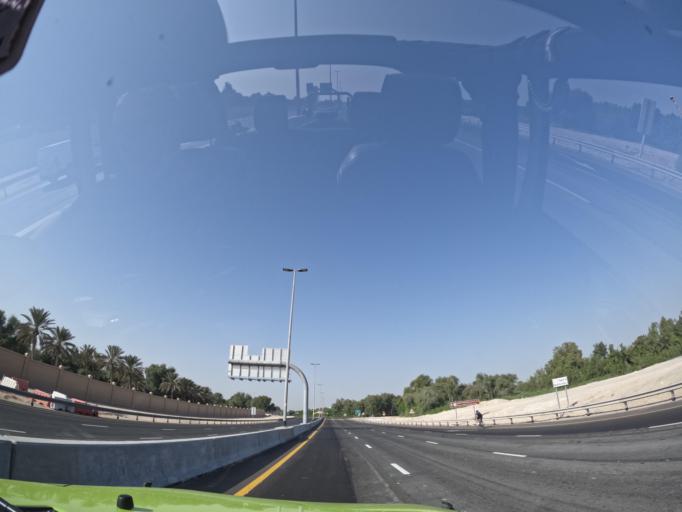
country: AE
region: Dubai
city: Dubai
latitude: 25.1487
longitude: 55.3332
